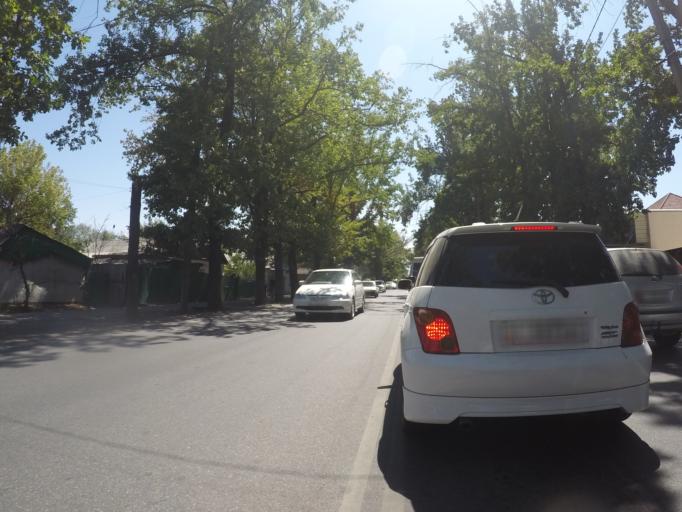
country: KG
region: Chuy
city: Bishkek
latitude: 42.8524
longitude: 74.5770
